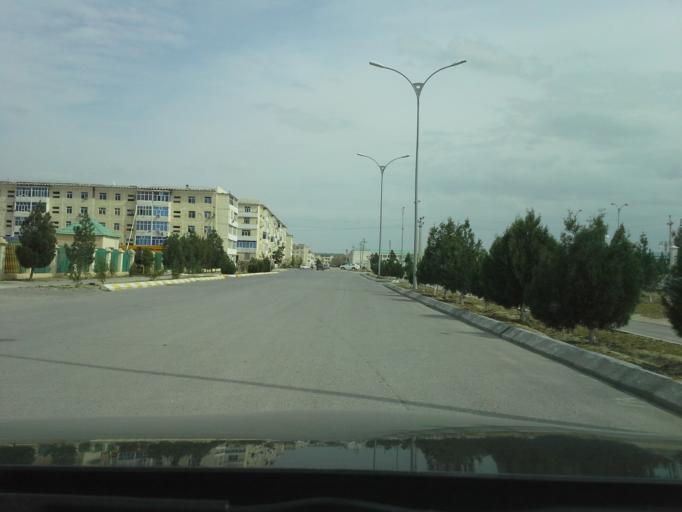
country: TM
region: Ahal
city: Abadan
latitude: 38.0530
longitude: 58.1473
